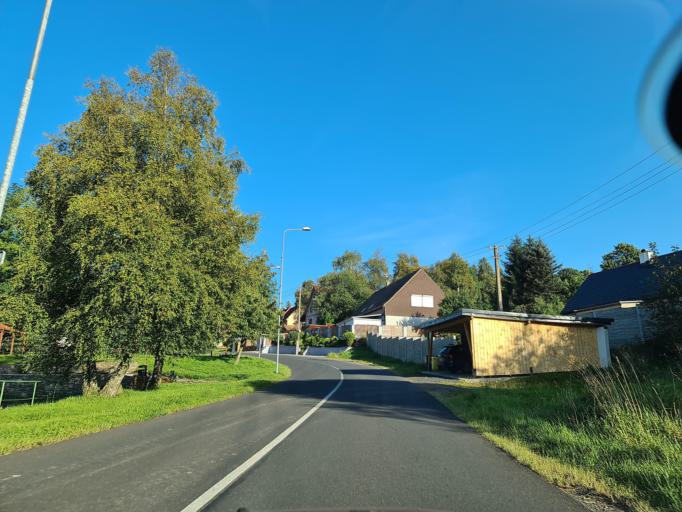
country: DE
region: Saxony
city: Deutschneudorf
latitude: 50.5992
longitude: 13.4708
